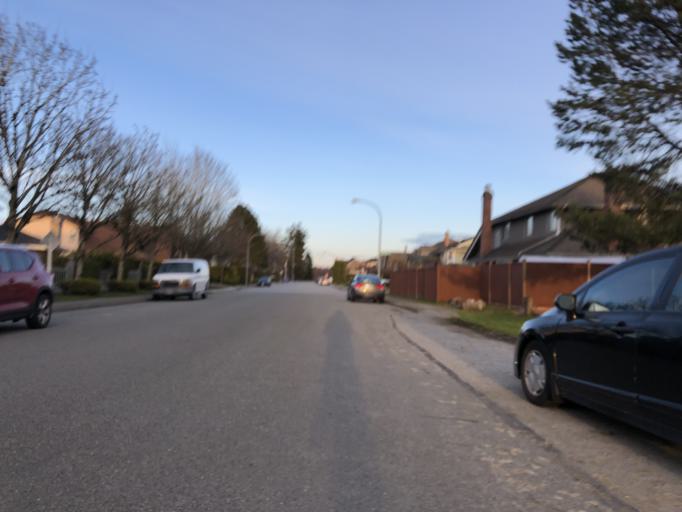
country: CA
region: British Columbia
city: Richmond
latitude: 49.1517
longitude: -123.1172
